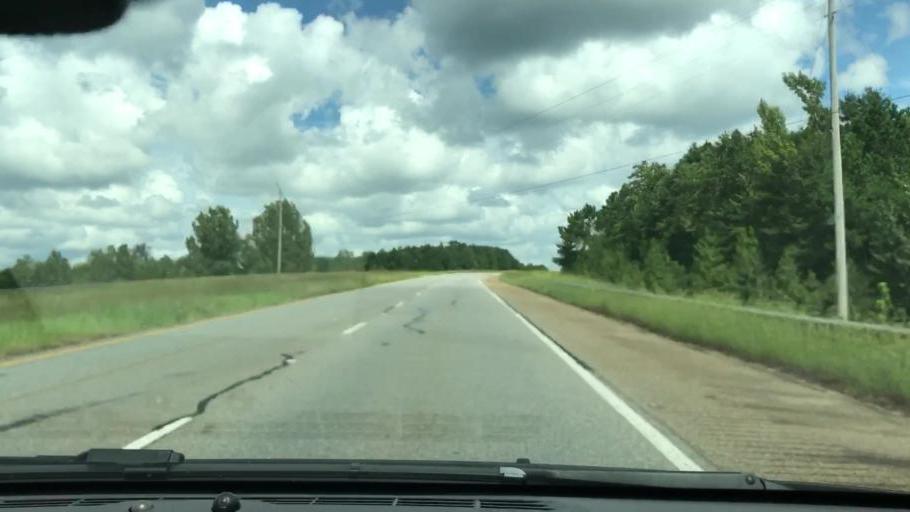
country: US
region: Georgia
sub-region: Stewart County
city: Lumpkin
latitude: 32.1100
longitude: -84.8138
